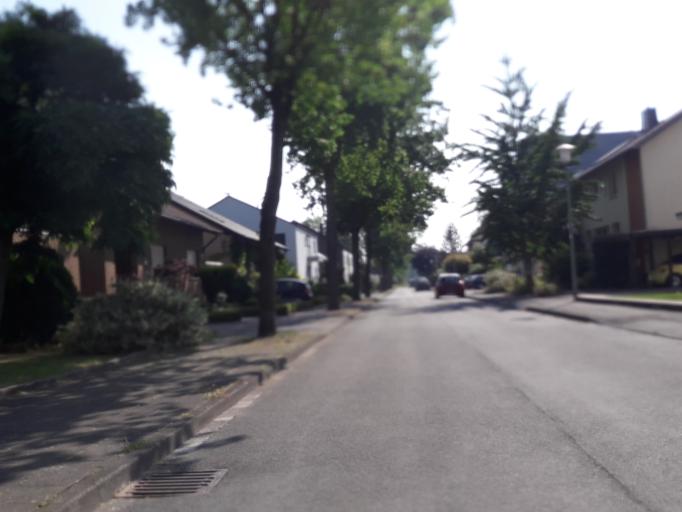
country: DE
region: North Rhine-Westphalia
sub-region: Regierungsbezirk Detmold
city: Paderborn
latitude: 51.6845
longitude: 8.6852
